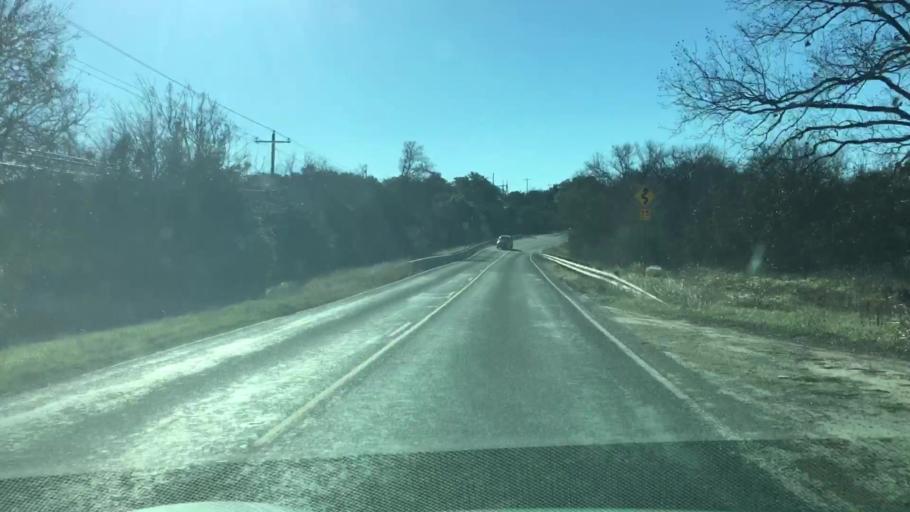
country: US
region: Texas
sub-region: Blanco County
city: Blanco
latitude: 30.0873
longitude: -98.4142
